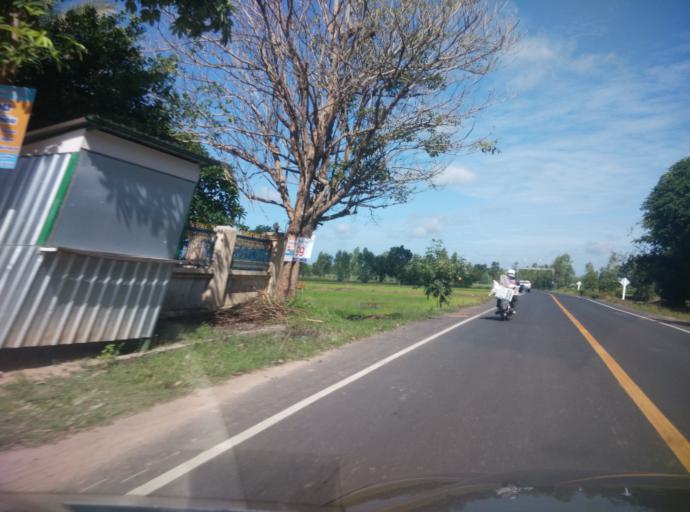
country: TH
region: Sisaket
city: Uthumphon Phisai
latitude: 15.1244
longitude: 104.1982
